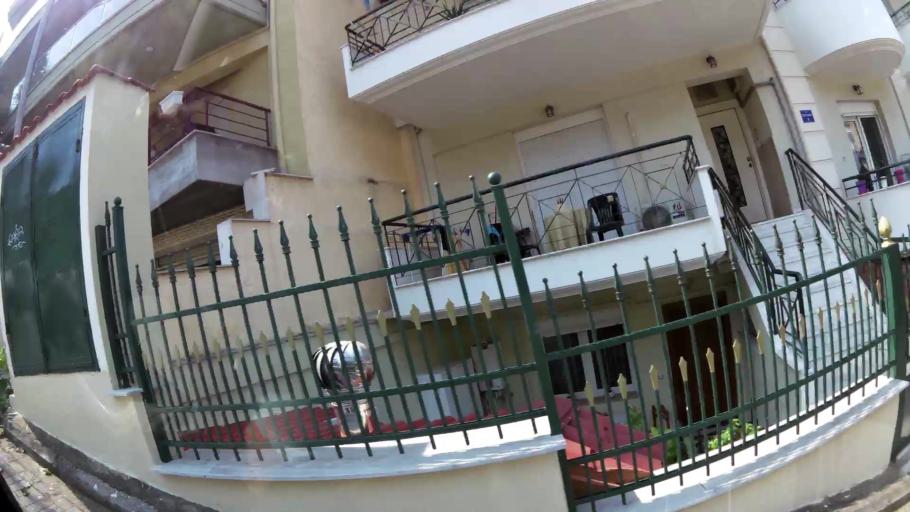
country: GR
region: Central Macedonia
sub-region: Nomos Thessalonikis
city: Agios Pavlos
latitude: 40.6448
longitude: 22.9560
